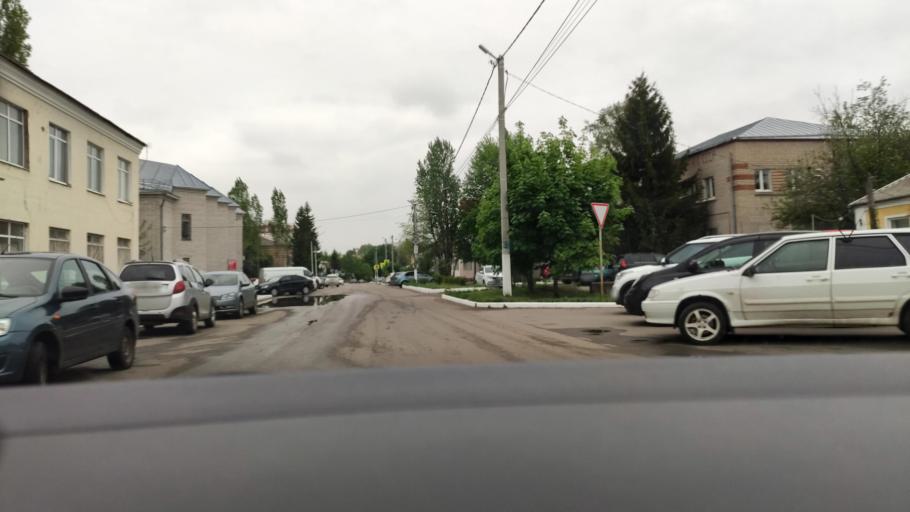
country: RU
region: Voronezj
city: Novaya Usman'
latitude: 51.6432
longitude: 39.4162
